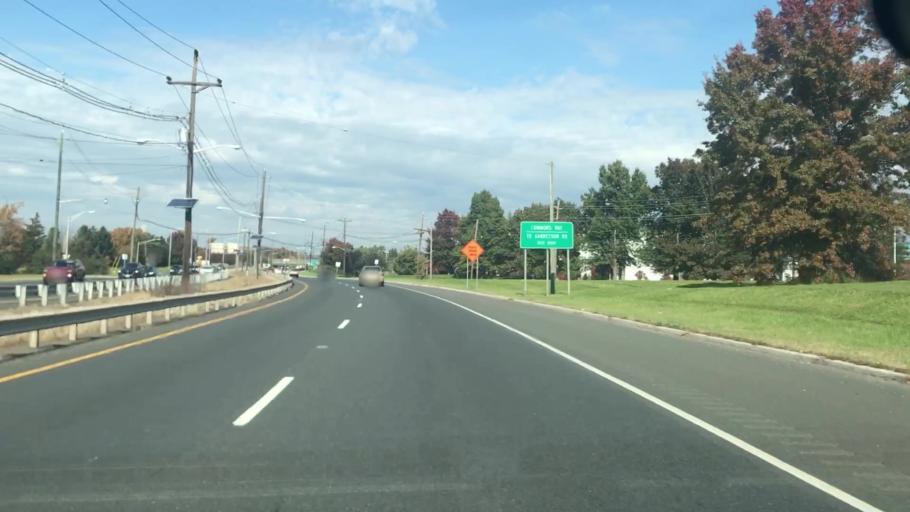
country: US
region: New Jersey
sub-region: Somerset County
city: Somerville
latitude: 40.5834
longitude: -74.6217
